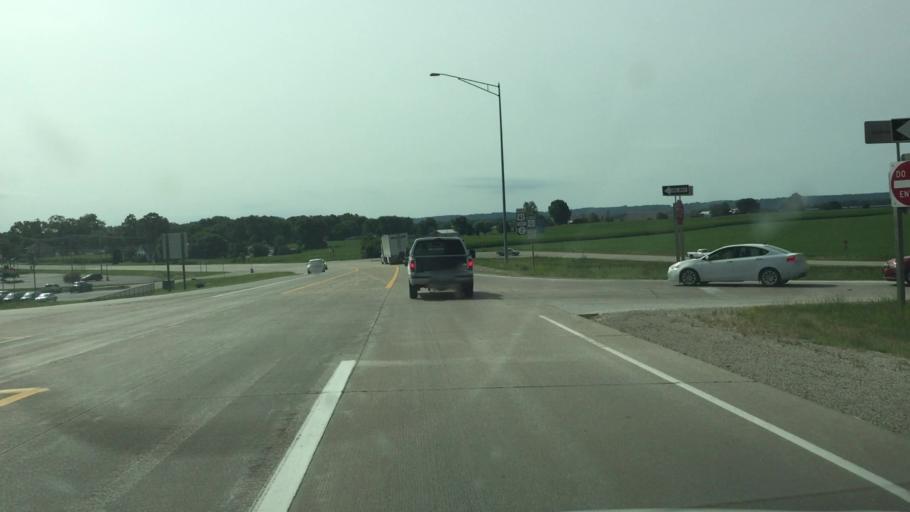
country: US
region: Illinois
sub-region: Hancock County
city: Nauvoo
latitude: 40.6256
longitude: -91.3976
